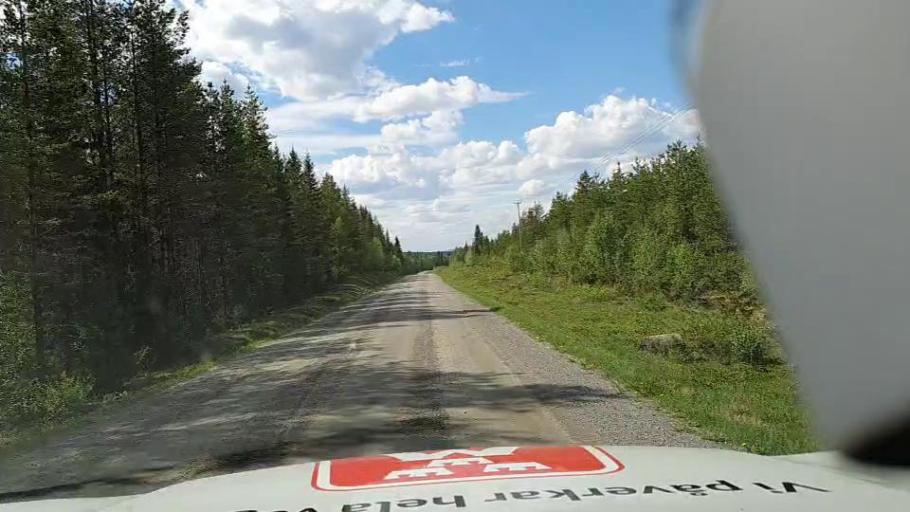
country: SE
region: Vaesterbotten
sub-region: Vilhelmina Kommun
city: Sjoberg
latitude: 64.5420
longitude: 15.6676
